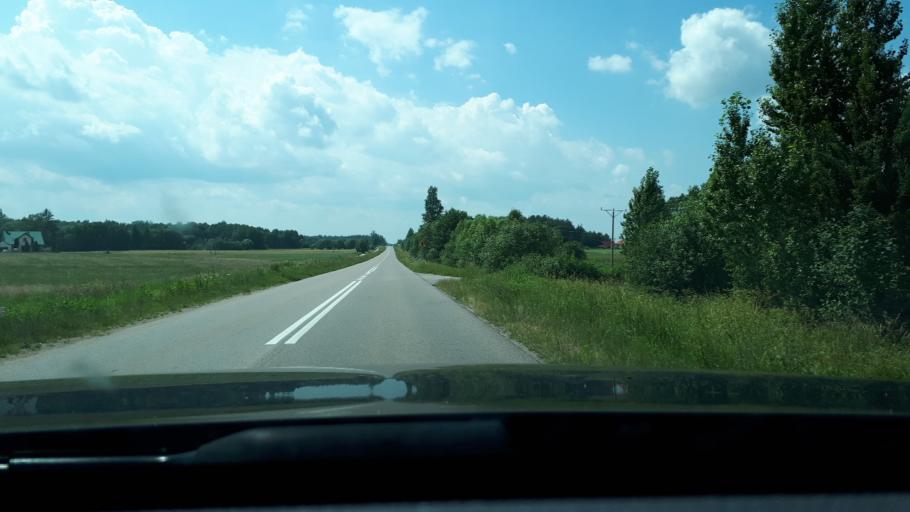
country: PL
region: Podlasie
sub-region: Powiat bialostocki
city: Choroszcz
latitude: 53.1282
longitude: 23.0034
